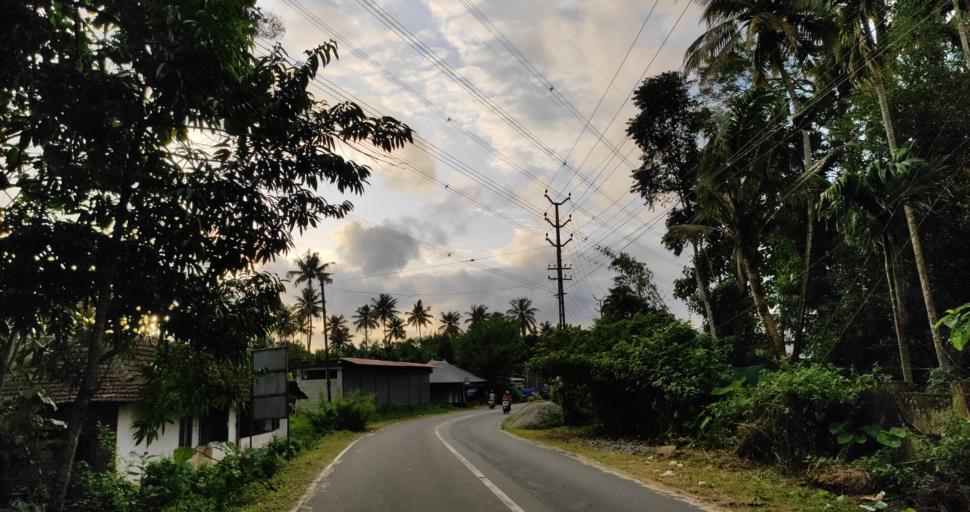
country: IN
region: Kerala
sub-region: Thrissur District
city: Kizhake Chalakudi
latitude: 10.3123
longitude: 76.3893
